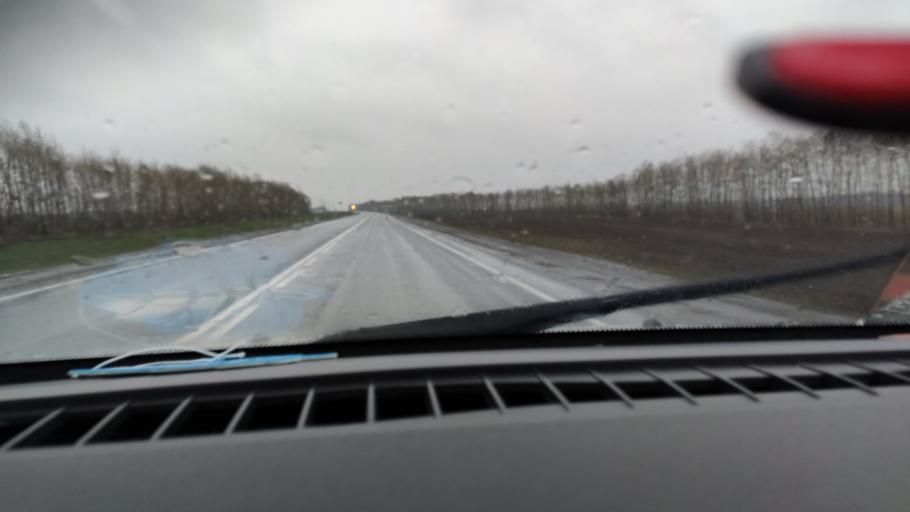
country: RU
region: Tatarstan
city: Mendeleyevsk
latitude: 55.9216
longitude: 52.2749
